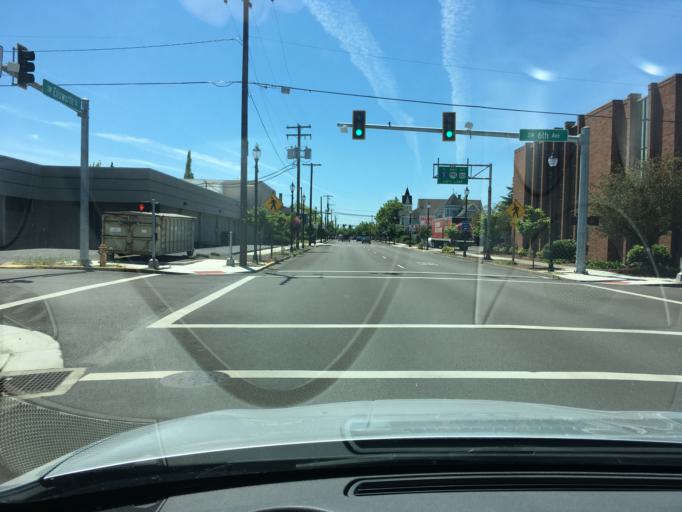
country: US
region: Oregon
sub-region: Linn County
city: Albany
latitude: 44.6335
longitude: -123.1053
